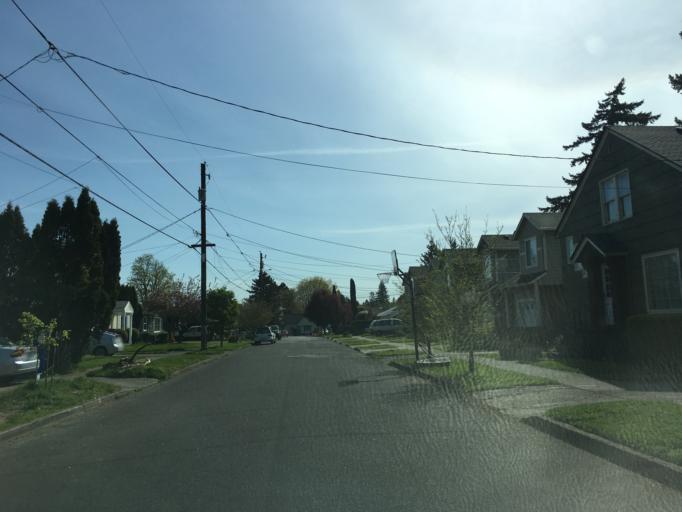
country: US
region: Oregon
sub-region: Multnomah County
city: Lents
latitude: 45.5302
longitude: -122.5757
